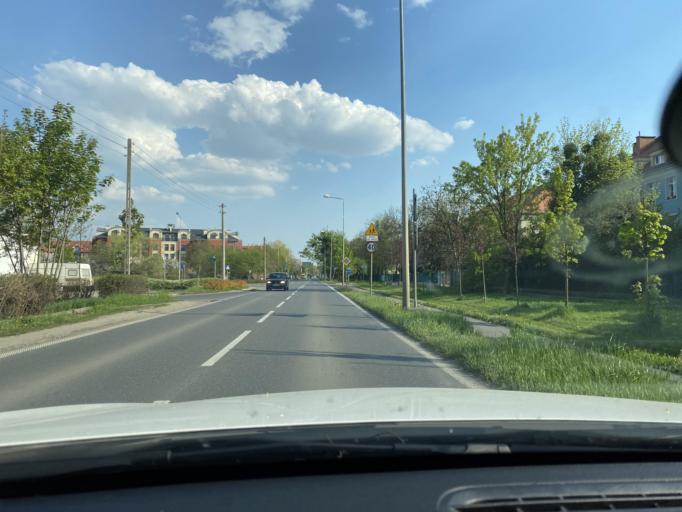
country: PL
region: Lower Silesian Voivodeship
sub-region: Powiat trzebnicki
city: Psary
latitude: 51.1452
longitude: 17.0229
